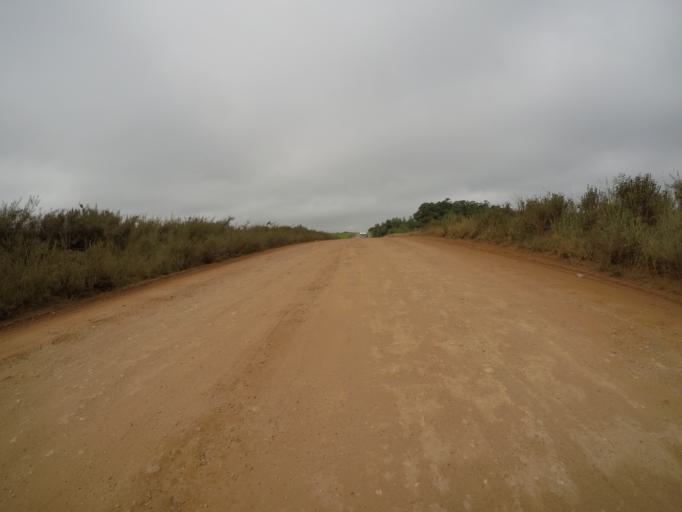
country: ZA
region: Eastern Cape
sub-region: Cacadu District Municipality
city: Kareedouw
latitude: -34.0136
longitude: 24.2377
